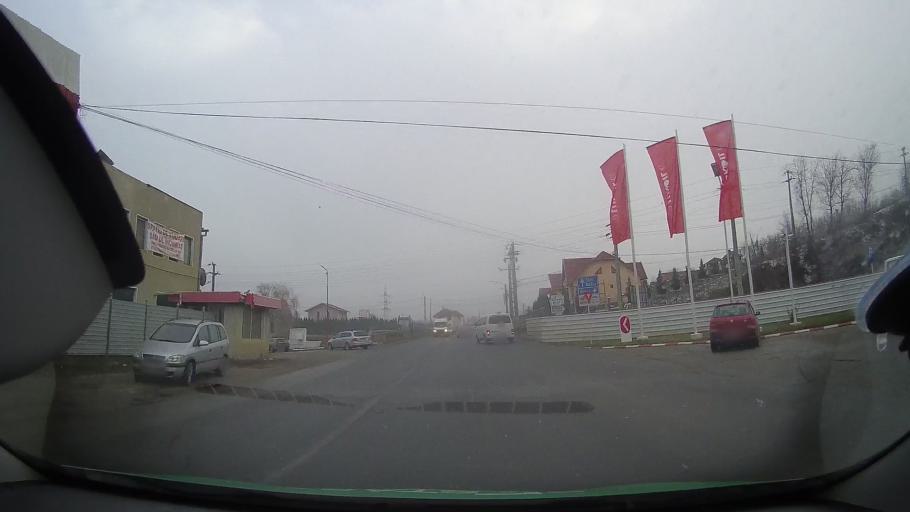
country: RO
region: Mures
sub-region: Municipiul Tarnaveni
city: Tarnaveni
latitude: 46.3154
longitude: 24.2973
